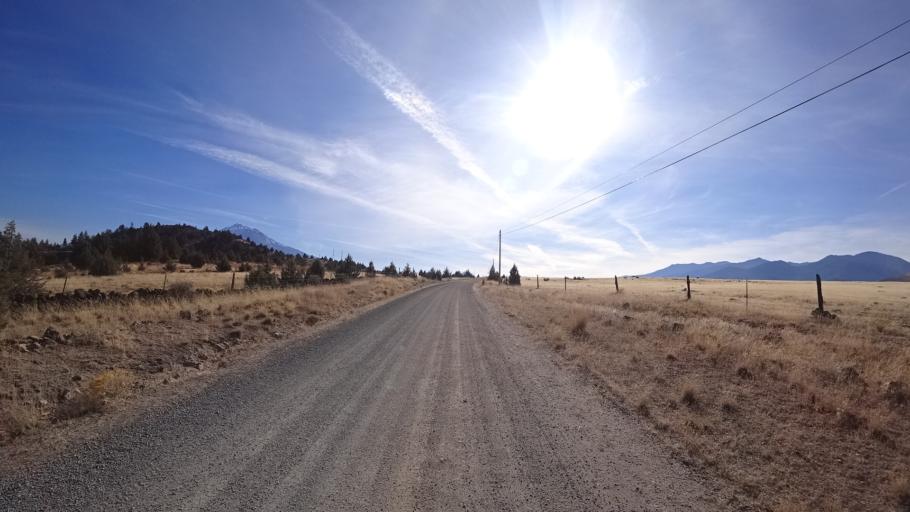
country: US
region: California
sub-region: Siskiyou County
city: Weed
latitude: 41.4937
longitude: -122.4524
